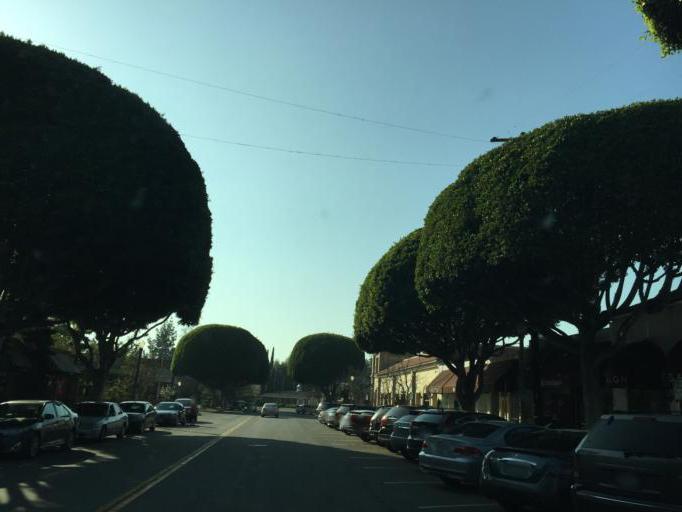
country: US
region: California
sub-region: Los Angeles County
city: South Pasadena
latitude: 34.1163
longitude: -118.1384
